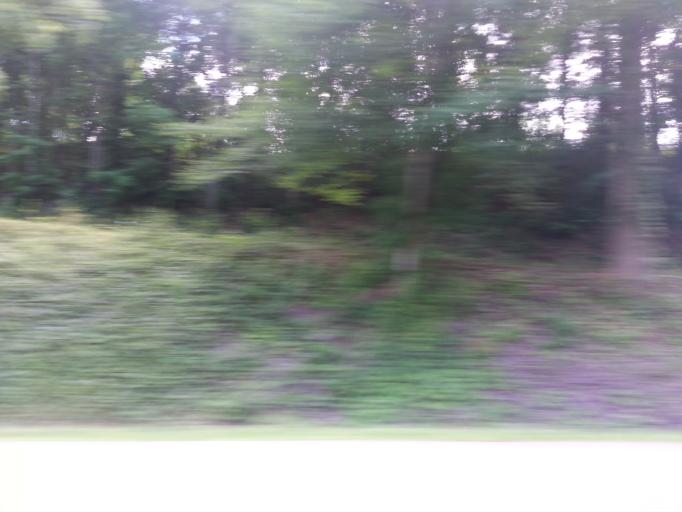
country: US
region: Virginia
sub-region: Lee County
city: Jonesville
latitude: 36.7618
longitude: -83.1202
